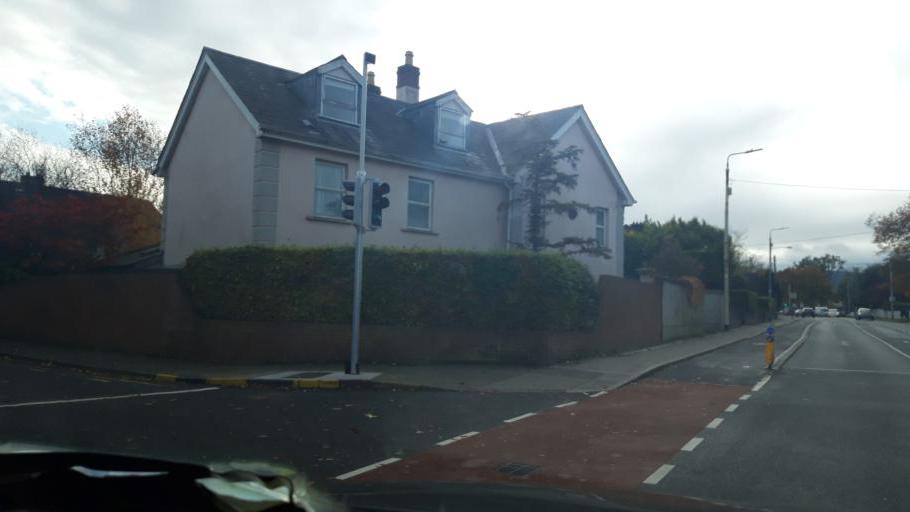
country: IE
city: Clonskeagh
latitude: 53.3076
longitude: -6.2368
